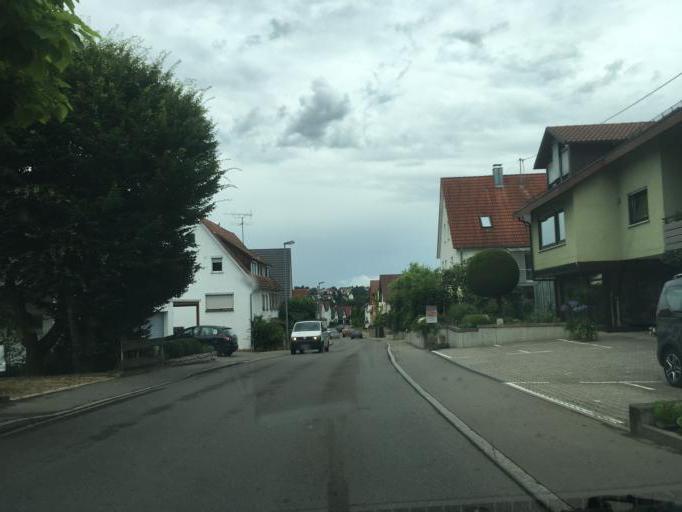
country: DE
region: Baden-Wuerttemberg
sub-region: Tuebingen Region
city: Sickenhausen
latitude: 48.5331
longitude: 9.2006
